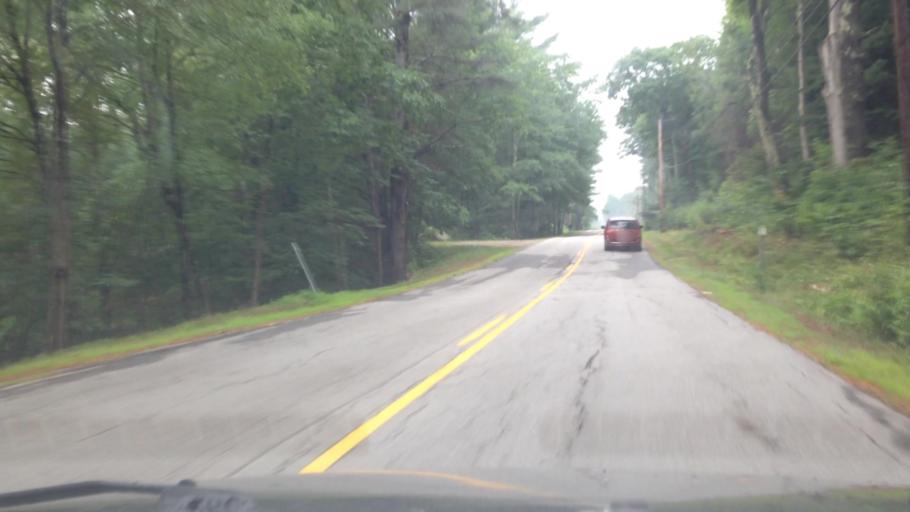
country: US
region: New Hampshire
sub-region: Cheshire County
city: Swanzey
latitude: 42.8627
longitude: -72.2449
